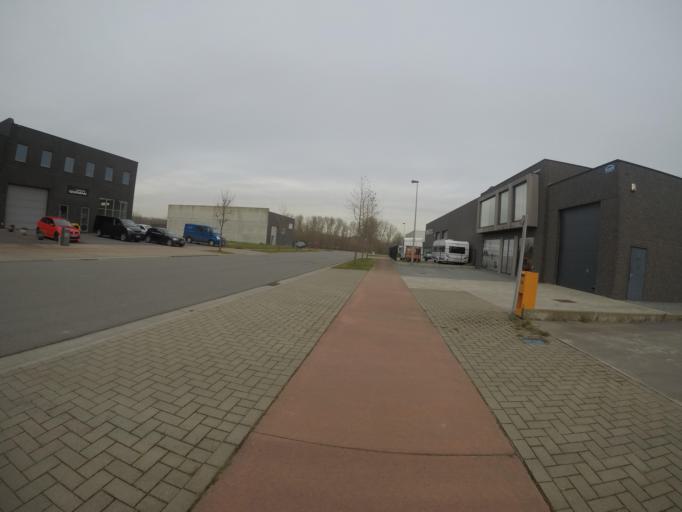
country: BE
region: Flanders
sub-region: Provincie Oost-Vlaanderen
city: Sint-Maria-Lierde
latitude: 50.8221
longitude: 3.8533
